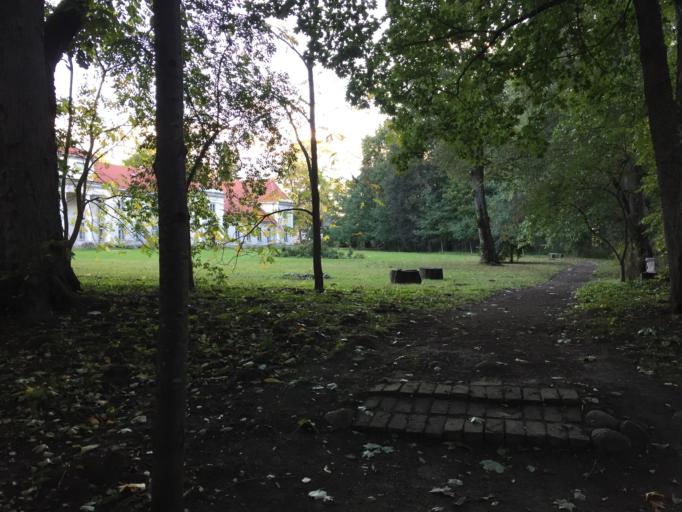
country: LV
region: Varaklani
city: Varaklani
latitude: 56.6084
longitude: 26.7766
